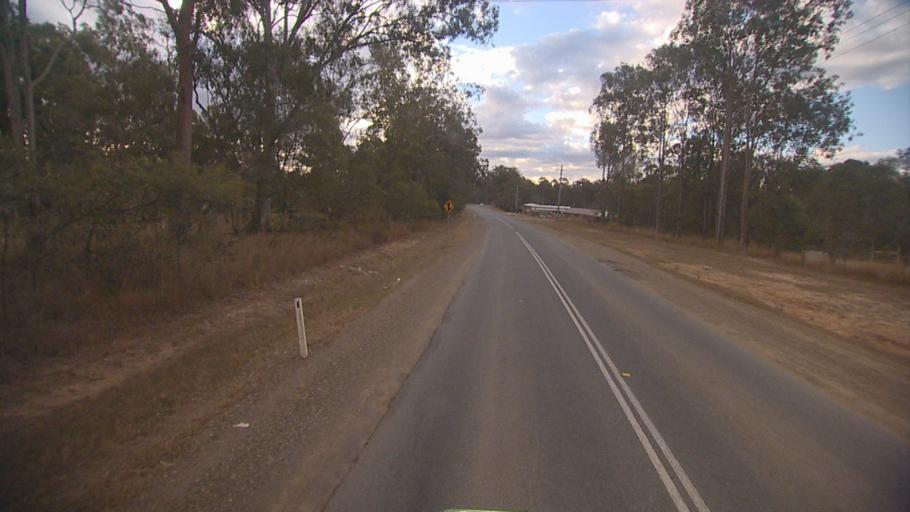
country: AU
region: Queensland
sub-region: Logan
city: Cedar Vale
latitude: -27.8558
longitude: 153.0533
